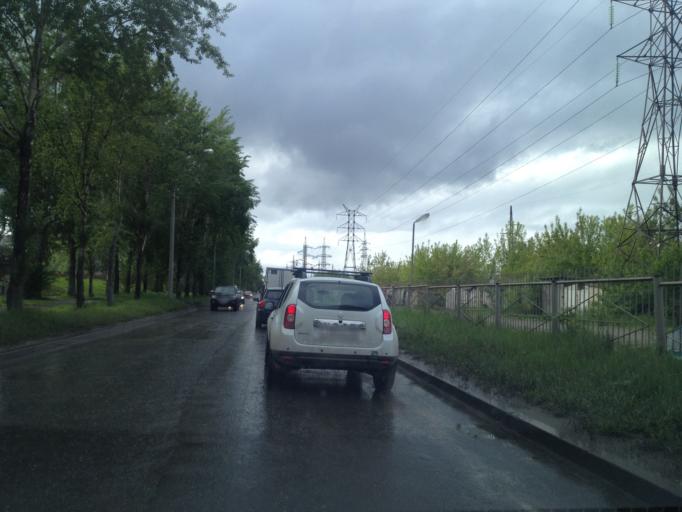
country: RU
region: Sverdlovsk
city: Yekaterinburg
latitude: 56.8695
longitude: 60.5640
